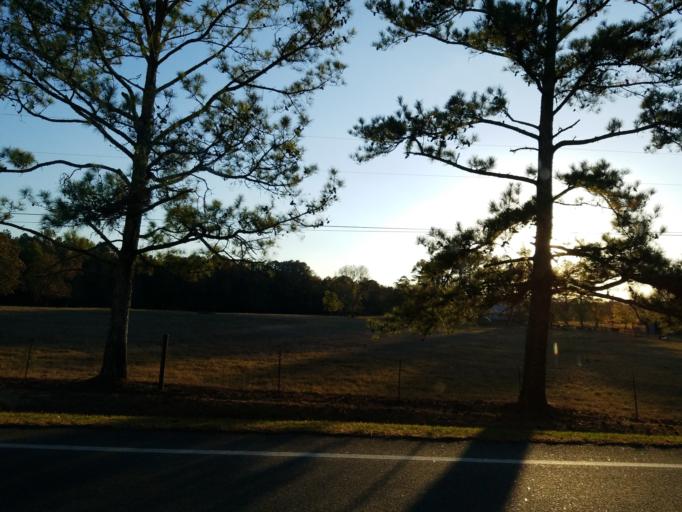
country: US
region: Georgia
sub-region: Gordon County
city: Calhoun
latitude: 34.5393
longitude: -84.9820
